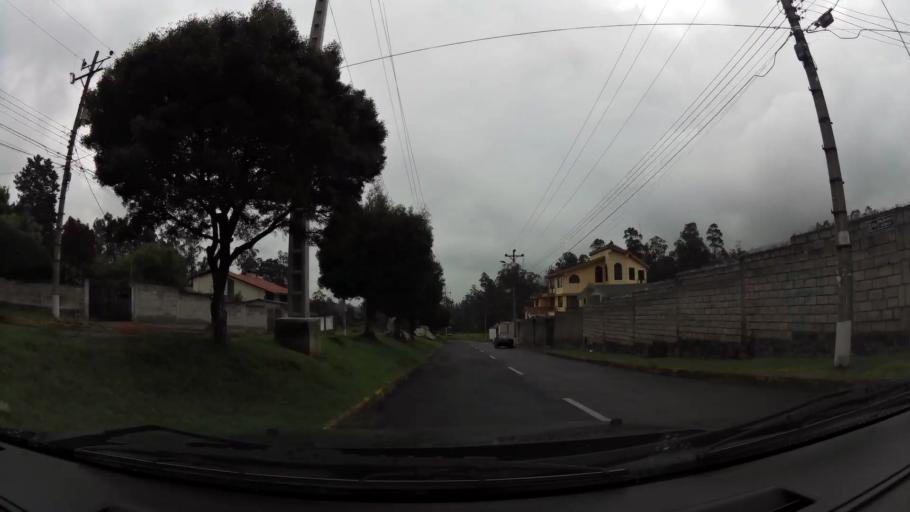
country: EC
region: Pichincha
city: Sangolqui
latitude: -0.2644
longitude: -78.4586
